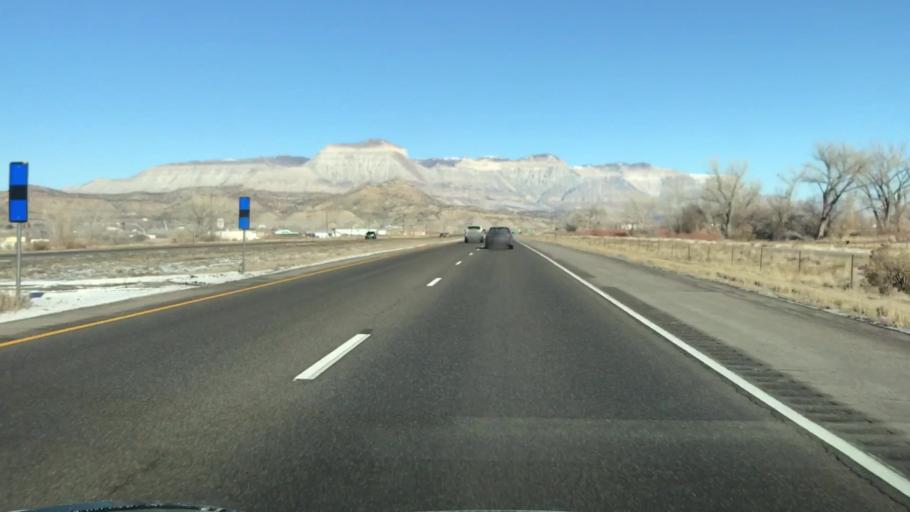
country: US
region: Colorado
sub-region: Garfield County
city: Parachute
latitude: 39.3143
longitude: -108.2129
